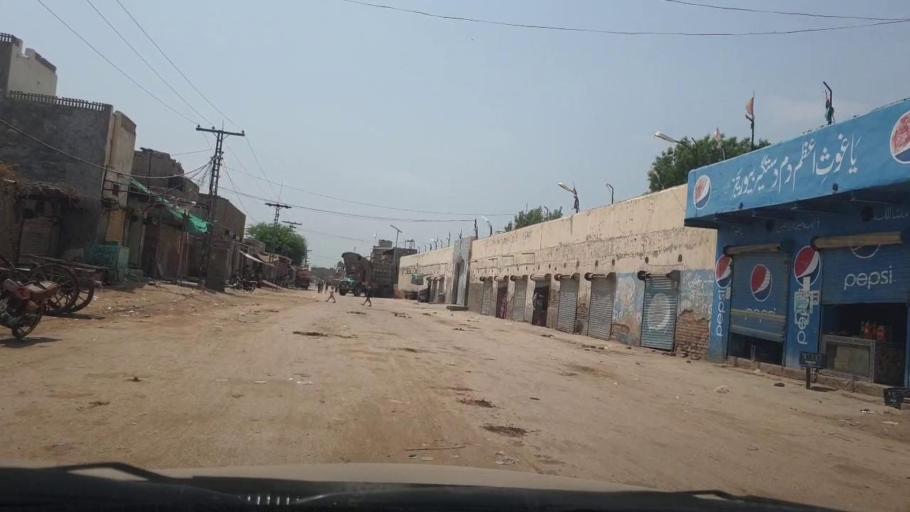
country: PK
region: Sindh
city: Ratodero
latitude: 27.7273
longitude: 68.2826
